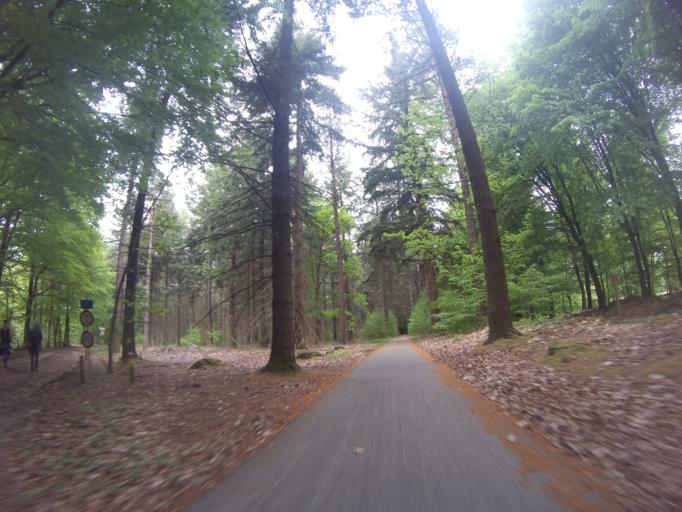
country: NL
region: Drenthe
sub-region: Gemeente Assen
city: Assen
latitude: 52.9185
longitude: 6.6559
